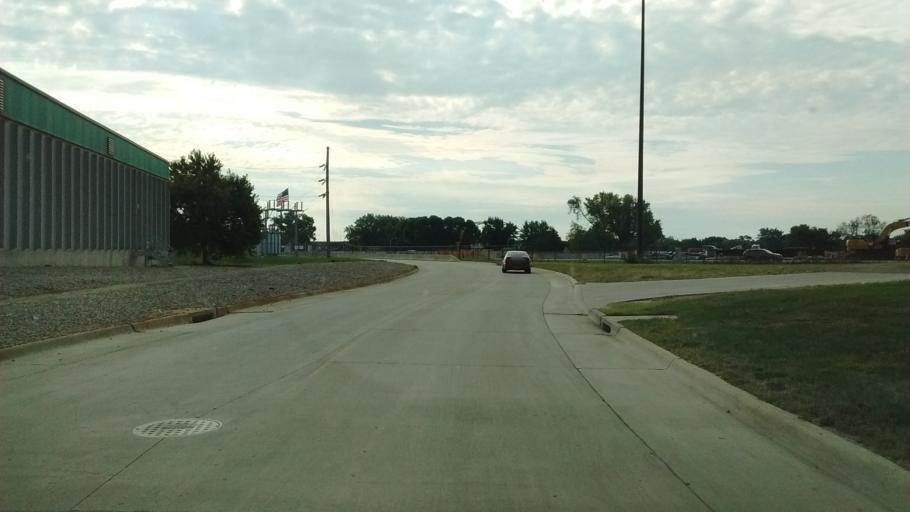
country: US
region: Nebraska
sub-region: Dakota County
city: South Sioux City
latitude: 42.4933
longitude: -96.4212
